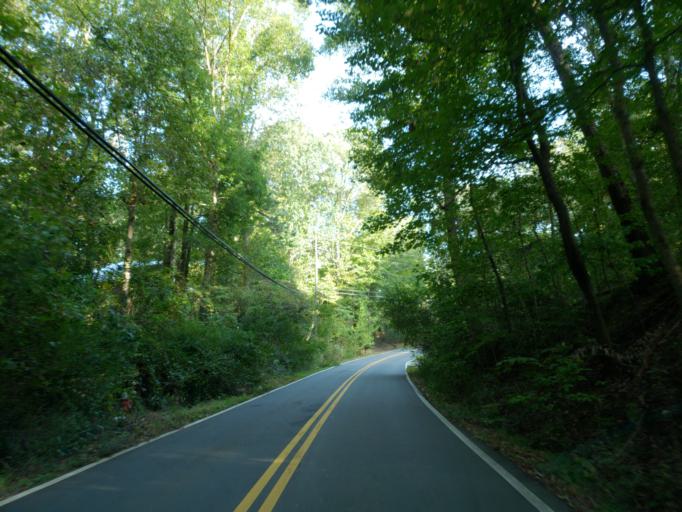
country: US
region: Georgia
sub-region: Fulton County
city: Roswell
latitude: 34.0802
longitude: -84.4149
